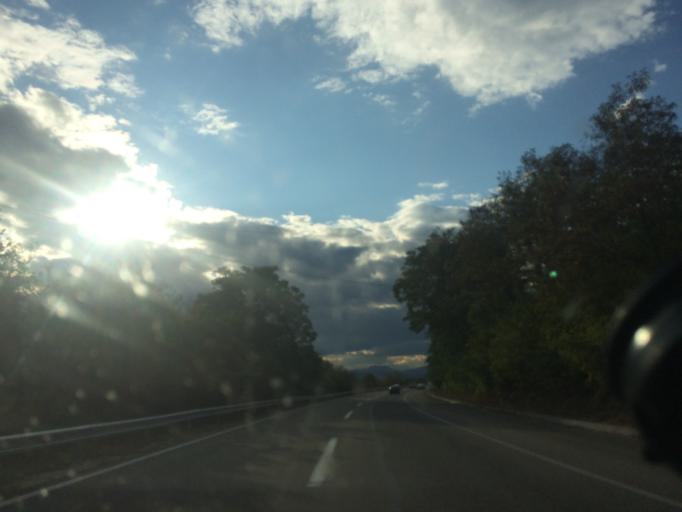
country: MK
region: Petrovec
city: Petrovec
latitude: 41.8948
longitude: 21.6747
